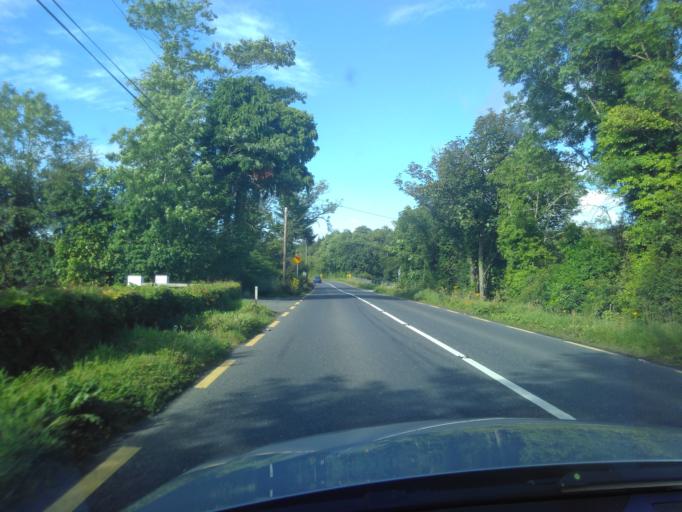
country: IE
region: Ulster
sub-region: County Donegal
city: Ballybofey
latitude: 54.8234
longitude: -7.7523
